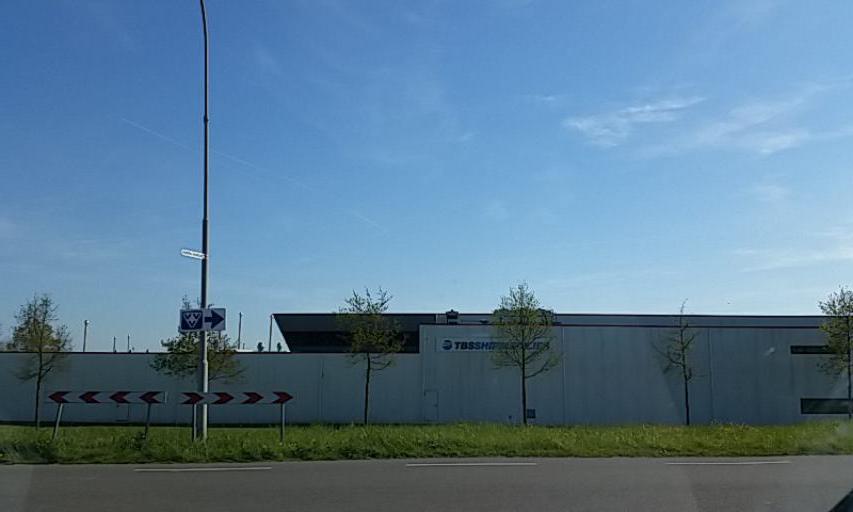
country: NL
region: Zeeland
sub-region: Gemeente Vlissingen
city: Vlissingen
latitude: 51.3941
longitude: 3.5716
